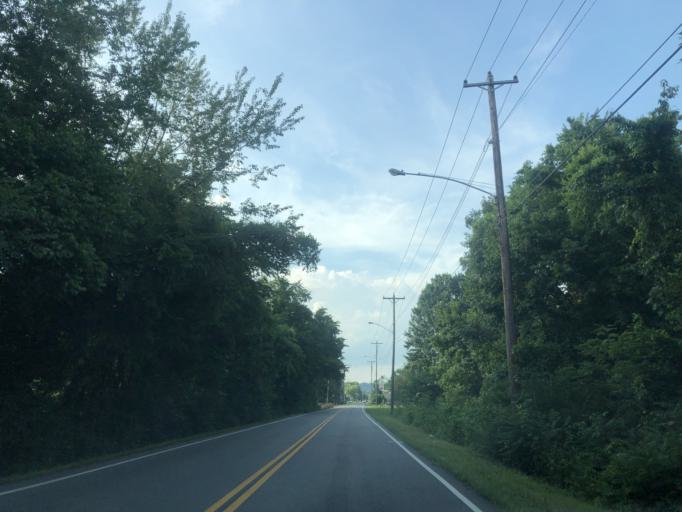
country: US
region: Tennessee
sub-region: Davidson County
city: Nashville
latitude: 36.2496
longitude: -86.8297
